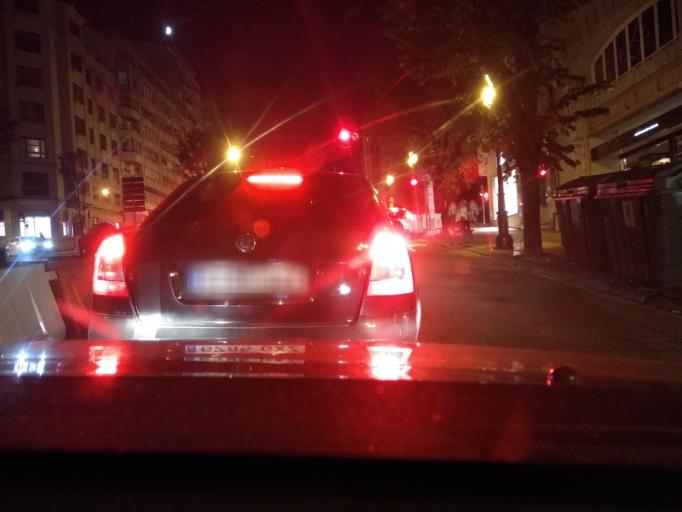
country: ES
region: Galicia
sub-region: Provincia de Pontevedra
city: Vigo
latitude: 42.2344
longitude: -8.7167
